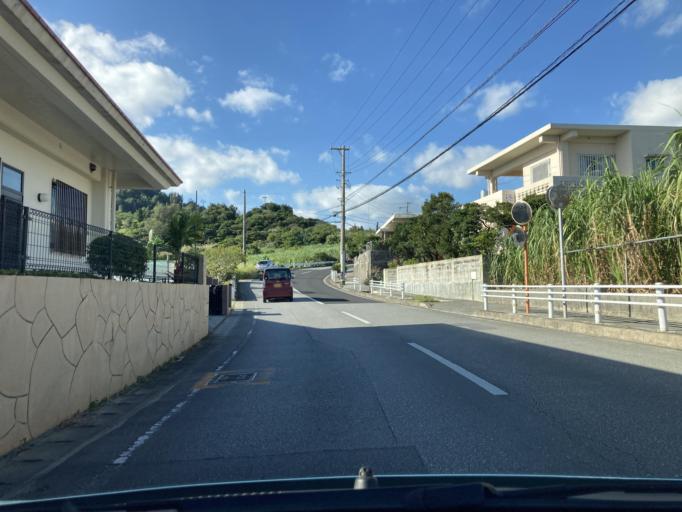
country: JP
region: Okinawa
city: Ginowan
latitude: 26.2180
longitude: 127.7530
